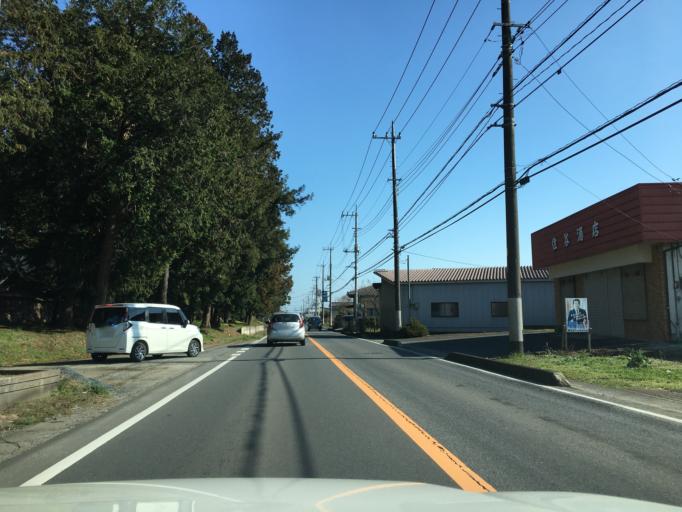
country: JP
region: Ibaraki
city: Omiya
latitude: 36.5196
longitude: 140.3621
